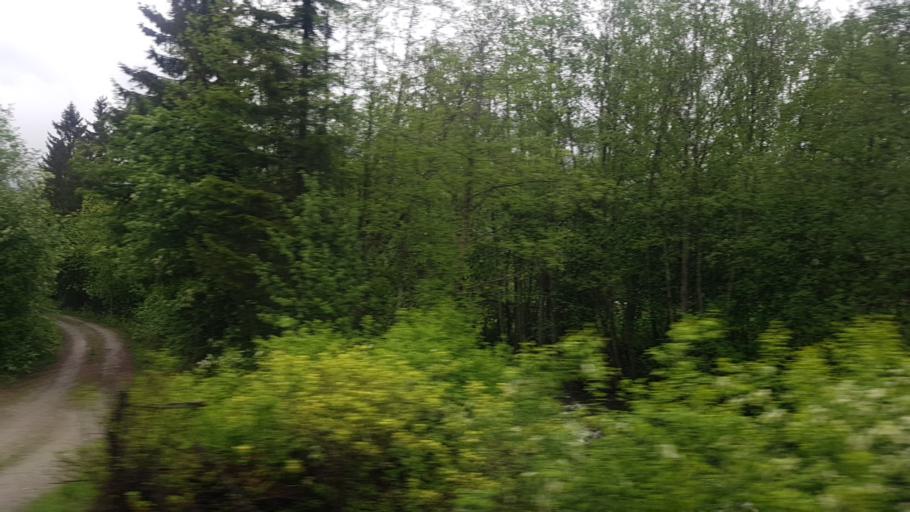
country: NO
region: Oppland
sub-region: Ringebu
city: Ringebu
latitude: 61.4353
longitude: 10.2089
